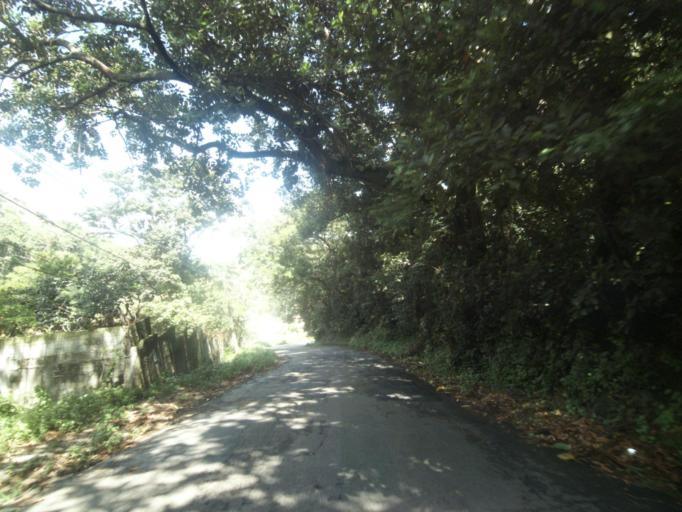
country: BR
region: Rio de Janeiro
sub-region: Niteroi
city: Niteroi
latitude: -22.9630
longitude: -43.0265
